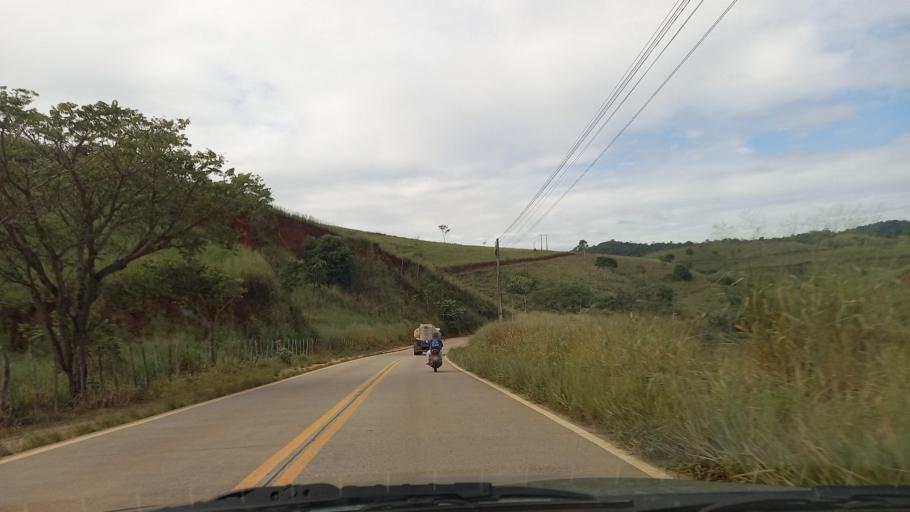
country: BR
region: Pernambuco
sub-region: Maraial
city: Maraial
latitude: -8.7475
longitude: -35.8058
